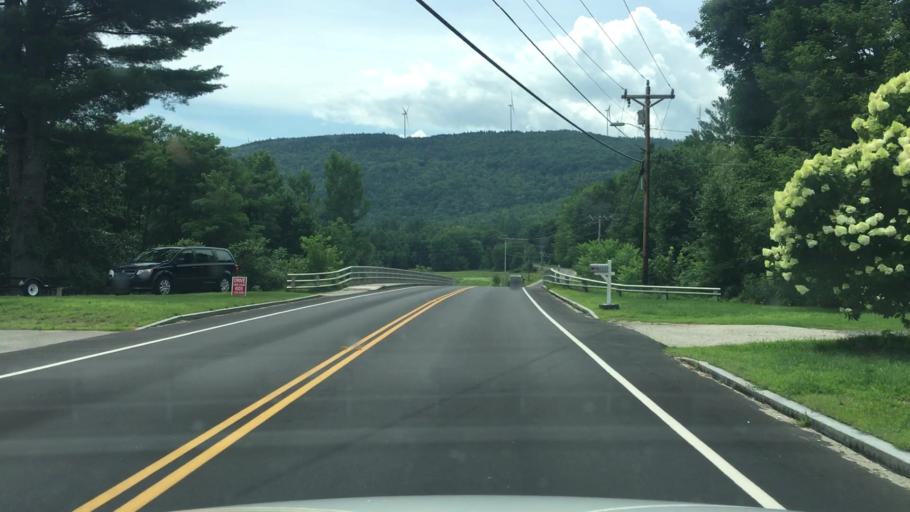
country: US
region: New Hampshire
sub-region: Grafton County
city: Rumney
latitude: 43.8017
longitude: -71.8140
